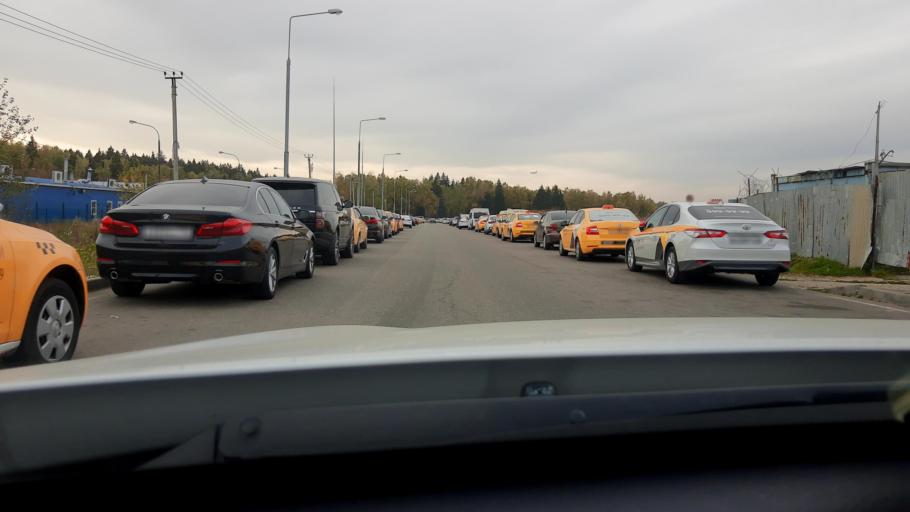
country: RU
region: Moskovskaya
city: Vostryakovo
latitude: 55.4660
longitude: 37.8526
